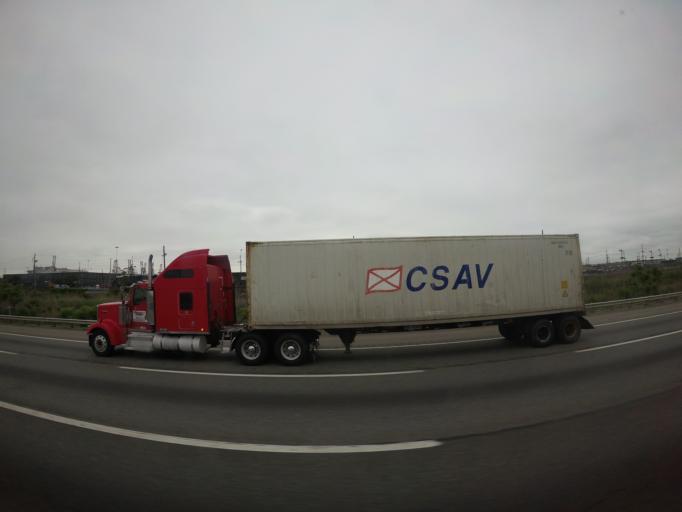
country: US
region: New Jersey
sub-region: Union County
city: Elizabeth
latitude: 40.6826
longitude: -74.1672
